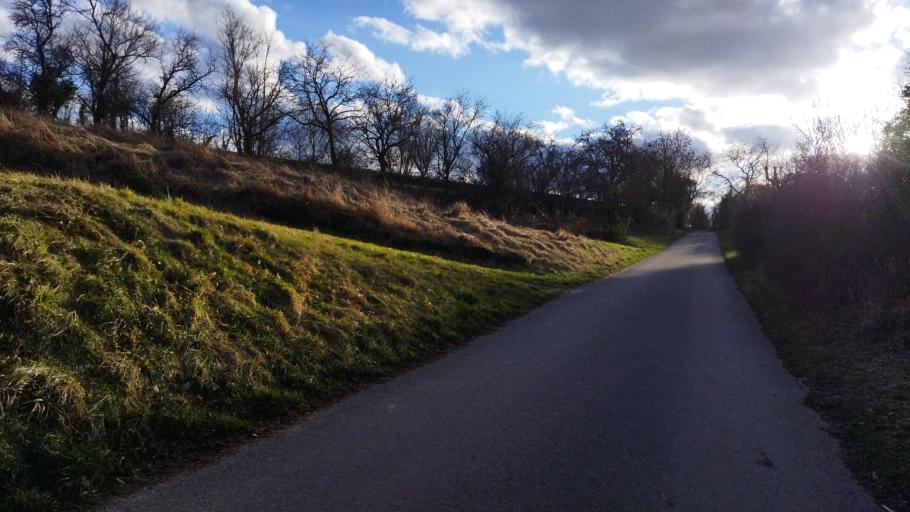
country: DE
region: Baden-Wuerttemberg
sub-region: Regierungsbezirk Stuttgart
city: Guglingen
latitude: 49.0746
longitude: 9.0037
